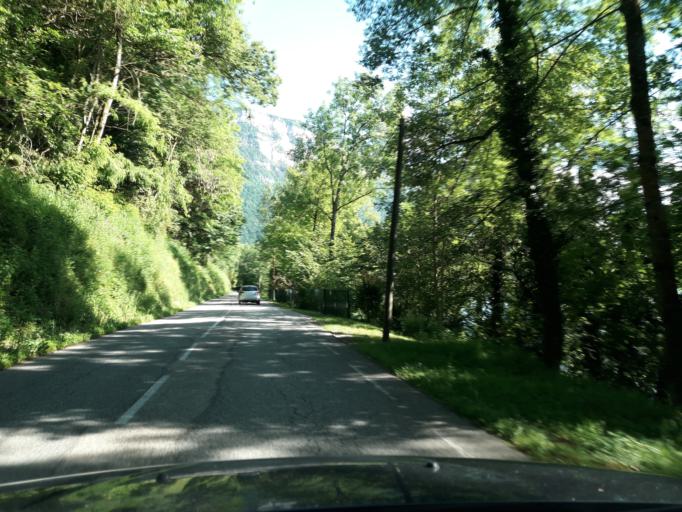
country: FR
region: Rhone-Alpes
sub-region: Departement de la Savoie
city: Vimines
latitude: 45.5509
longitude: 5.8097
